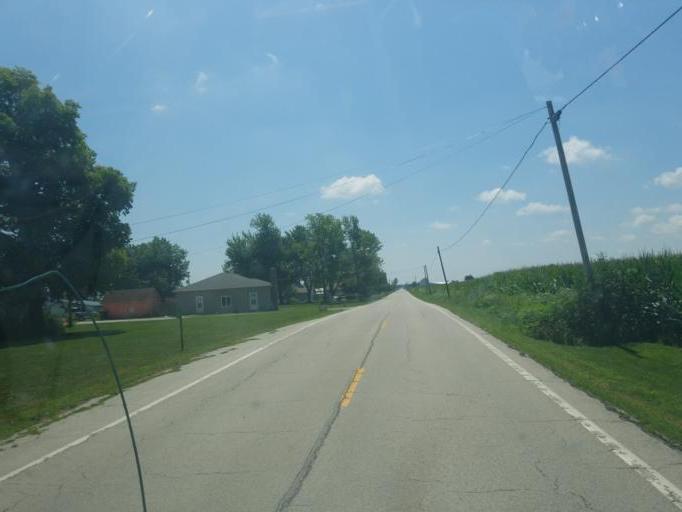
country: US
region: Ohio
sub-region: Allen County
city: Spencerville
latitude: 40.6963
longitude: -84.4256
